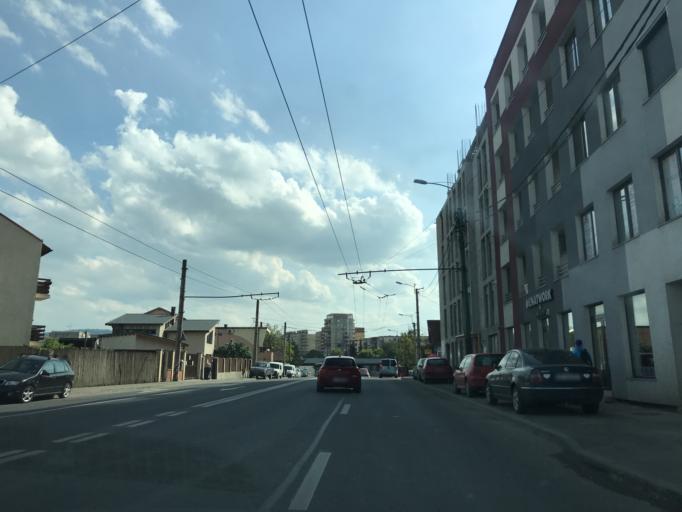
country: RO
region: Cluj
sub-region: Municipiul Cluj-Napoca
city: Cluj-Napoca
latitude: 46.7870
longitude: 23.6146
